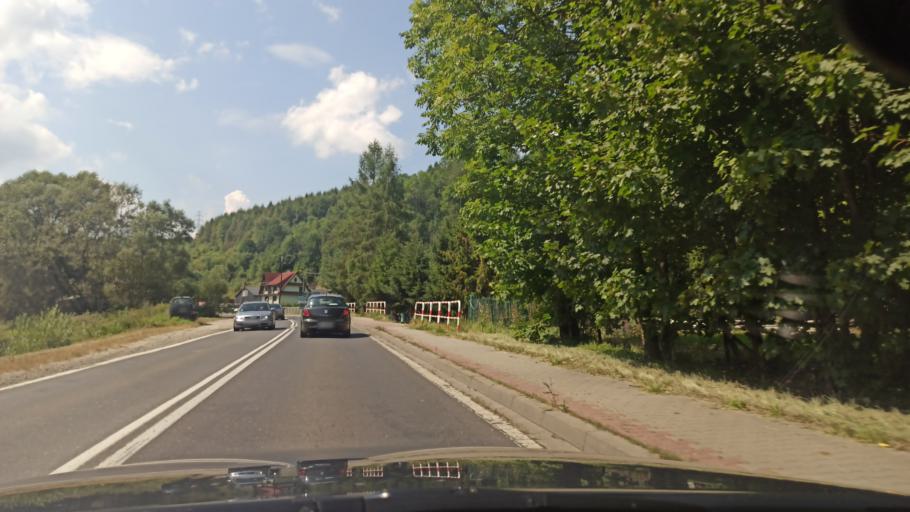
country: PL
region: Lesser Poland Voivodeship
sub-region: Powiat nowotarski
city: Kroscienko nad Dunajcem
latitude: 49.4389
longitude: 20.3886
